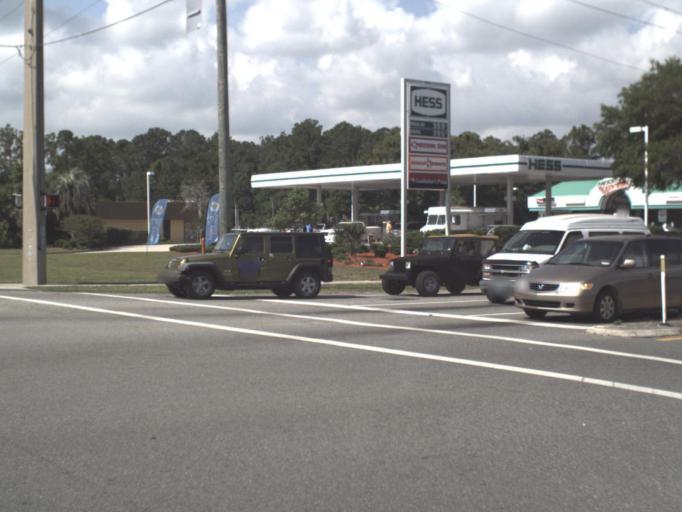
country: US
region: Florida
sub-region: Saint Johns County
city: Saint Augustine South
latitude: 29.8513
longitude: -81.3228
